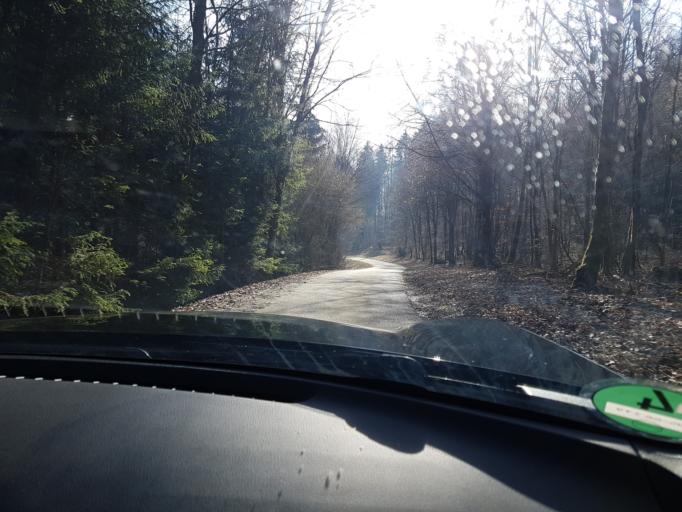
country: DE
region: Baden-Wuerttemberg
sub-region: Karlsruhe Region
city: Rosenberg
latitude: 49.4233
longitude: 9.4960
